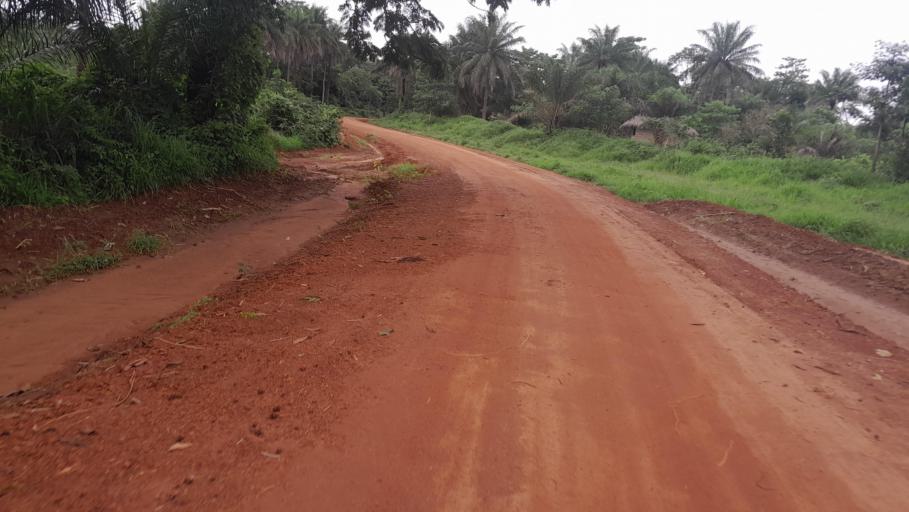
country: GN
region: Boke
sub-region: Boffa
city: Boffa
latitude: 10.0520
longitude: -13.8737
